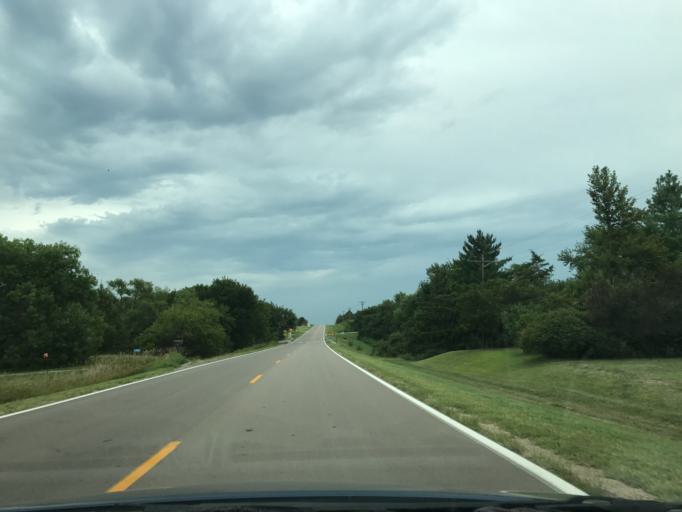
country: US
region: Nebraska
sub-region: Gage County
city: Beatrice
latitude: 40.2837
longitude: -96.8031
